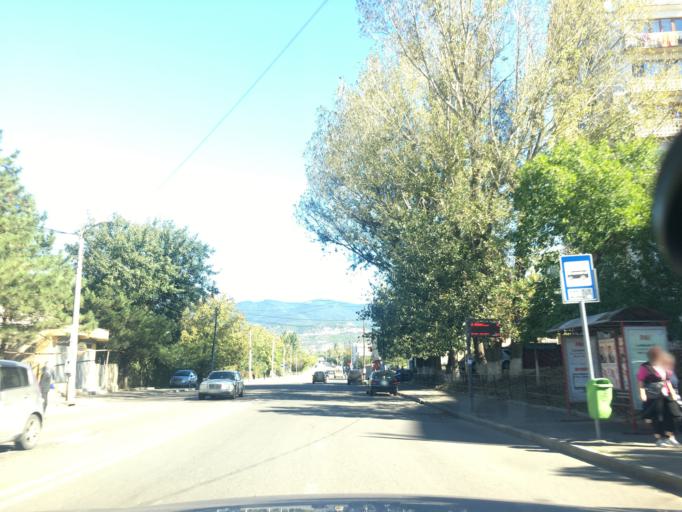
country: GE
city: Zahesi
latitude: 41.8007
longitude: 44.8136
